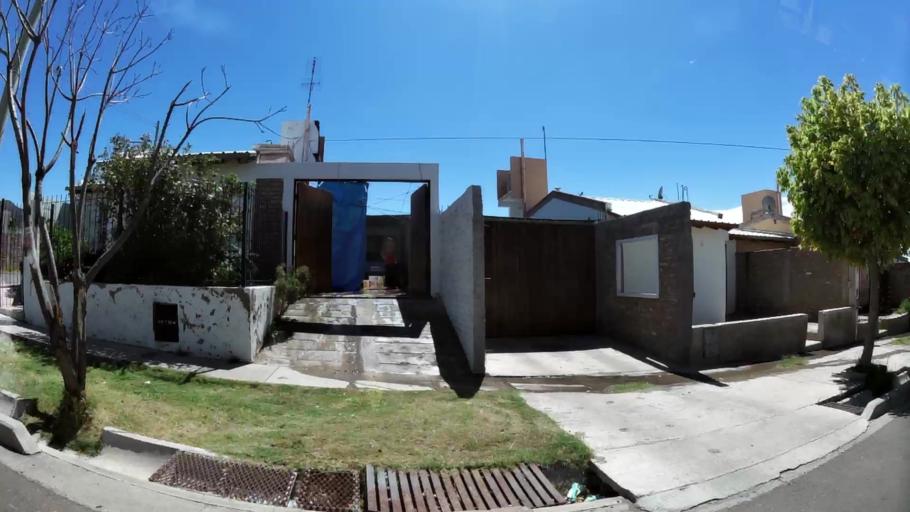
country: AR
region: Mendoza
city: Las Heras
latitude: -32.8508
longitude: -68.8744
